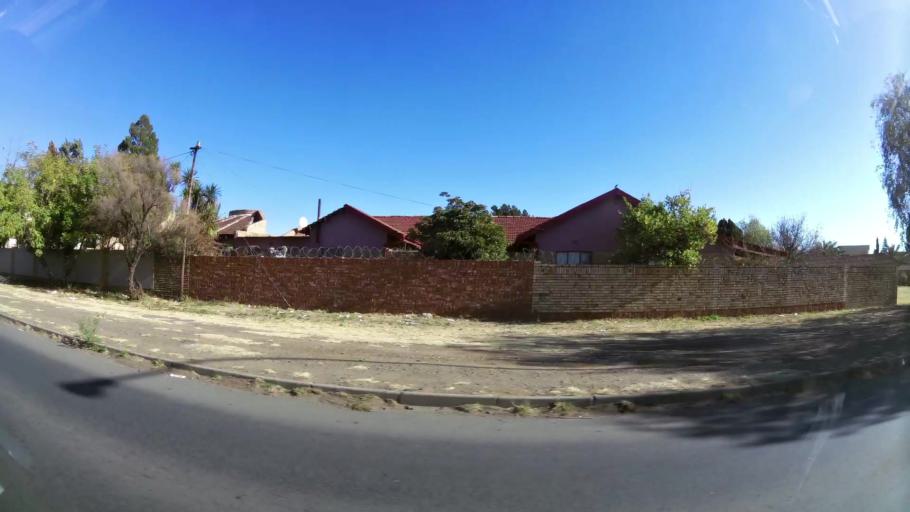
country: ZA
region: Northern Cape
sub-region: Frances Baard District Municipality
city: Kimberley
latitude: -28.7232
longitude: 24.7708
